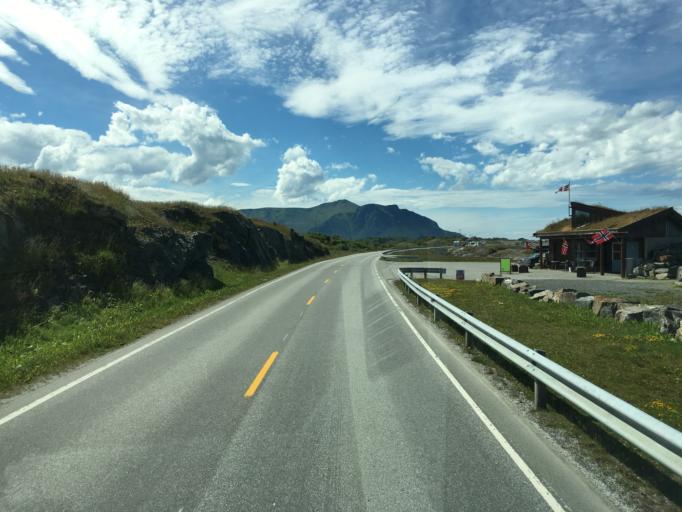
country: NO
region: More og Romsdal
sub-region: Eide
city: Eide
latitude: 63.0137
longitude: 7.3317
